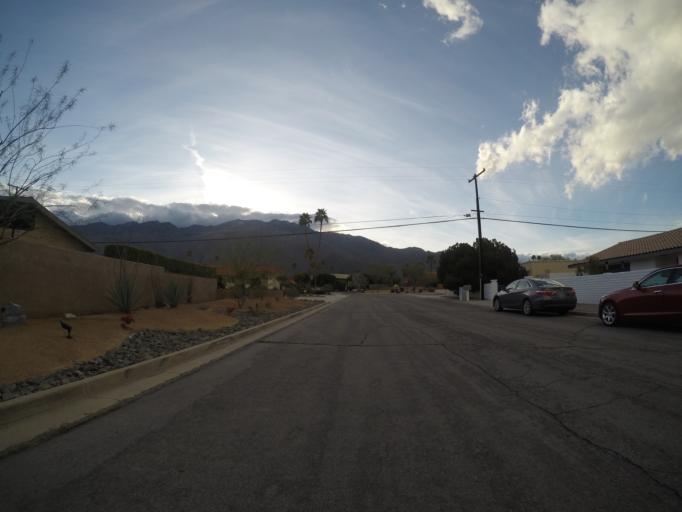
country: US
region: California
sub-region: Riverside County
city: Palm Springs
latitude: 33.8217
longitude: -116.5255
